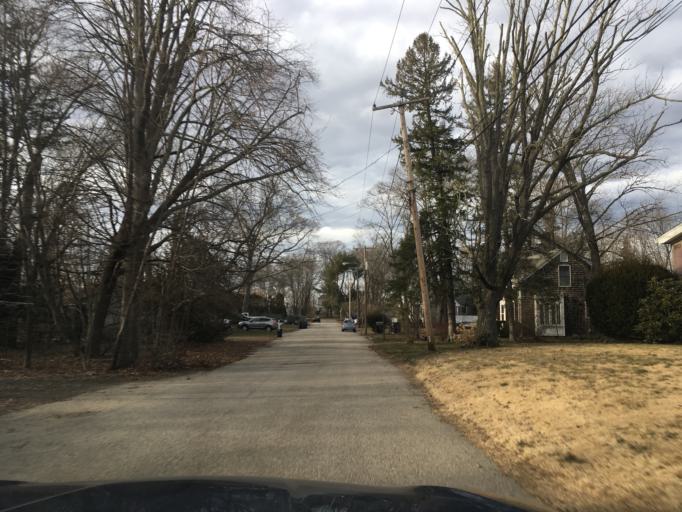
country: US
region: Rhode Island
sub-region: Kent County
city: East Greenwich
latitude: 41.6630
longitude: -71.4190
